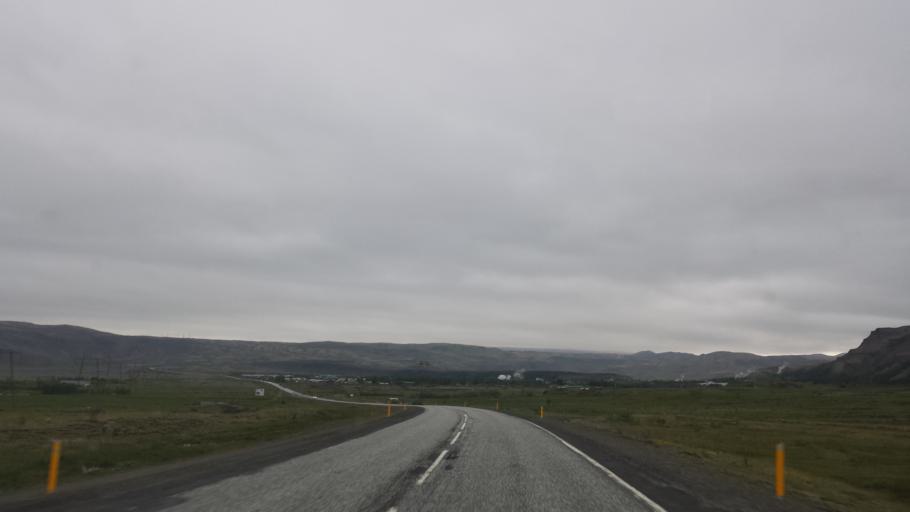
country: IS
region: South
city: Hveragerdi
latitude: 63.9846
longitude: -21.1582
